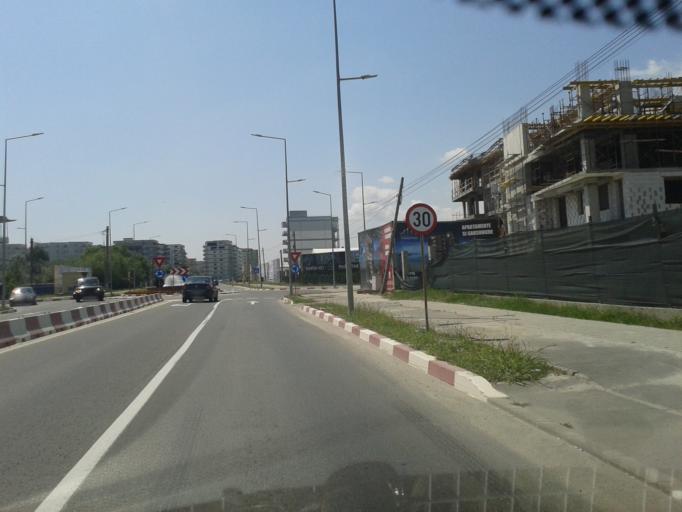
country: RO
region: Constanta
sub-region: Comuna Navodari
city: Navodari
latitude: 44.2770
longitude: 28.6173
